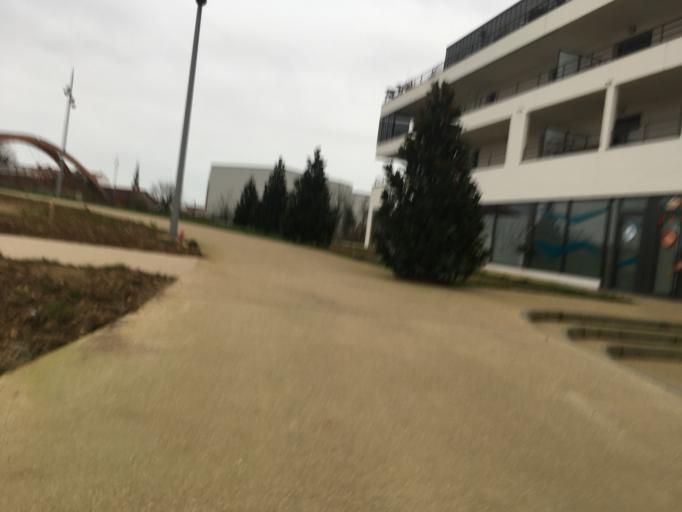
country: FR
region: Poitou-Charentes
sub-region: Departement de la Charente-Maritime
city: La Rochelle
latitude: 46.1673
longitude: -1.1441
